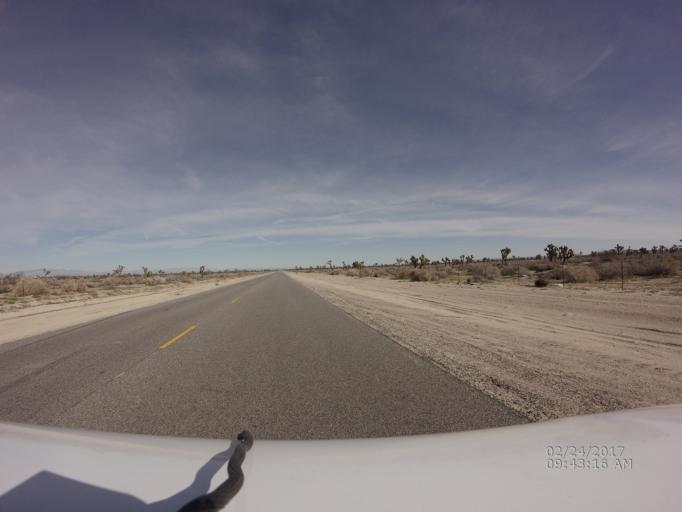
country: US
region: California
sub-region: Los Angeles County
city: Littlerock
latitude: 34.5849
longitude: -118.0050
